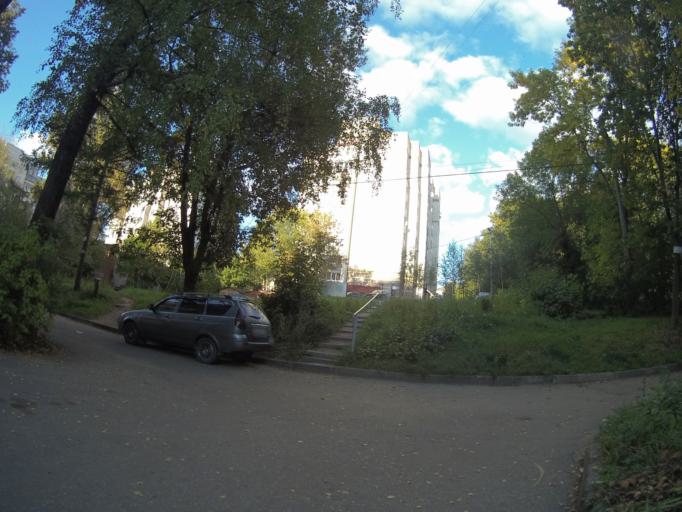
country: RU
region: Vladimir
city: Vladimir
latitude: 56.1147
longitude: 40.3454
